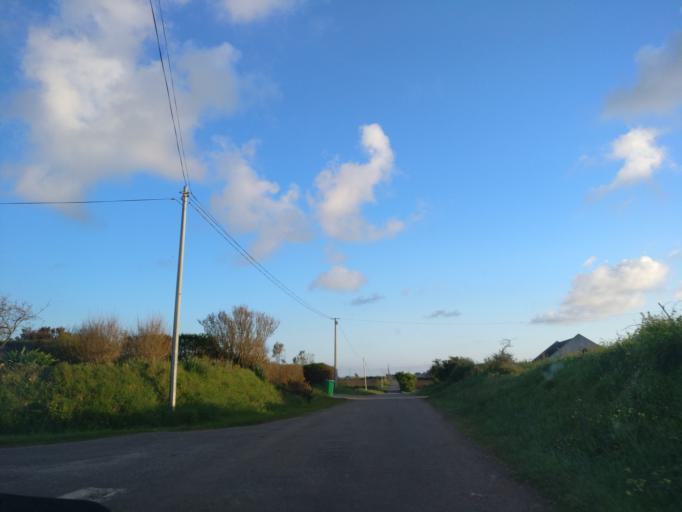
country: FR
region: Brittany
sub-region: Departement du Finistere
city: Lampaul-Plouarzel
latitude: 48.4571
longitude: -4.7550
